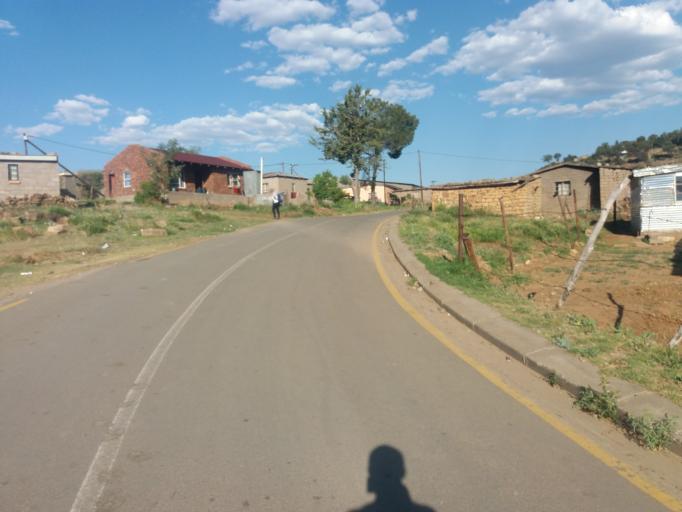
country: LS
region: Quthing
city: Quthing
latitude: -30.3991
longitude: 27.6981
